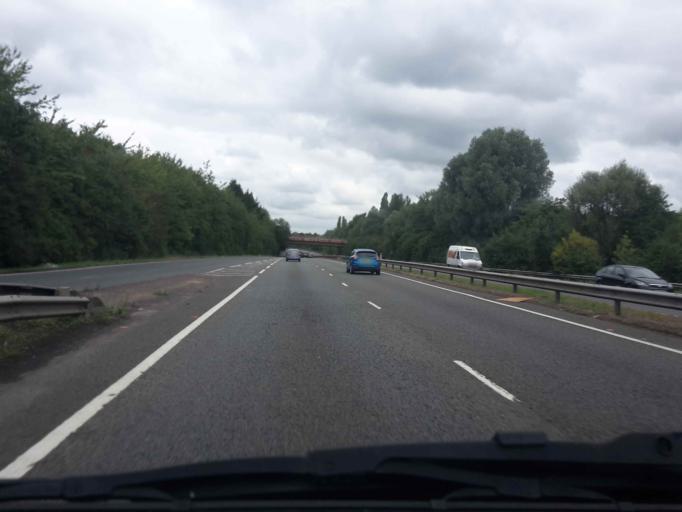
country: GB
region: England
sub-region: Hampshire
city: Farnborough
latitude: 51.2966
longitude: -0.7394
